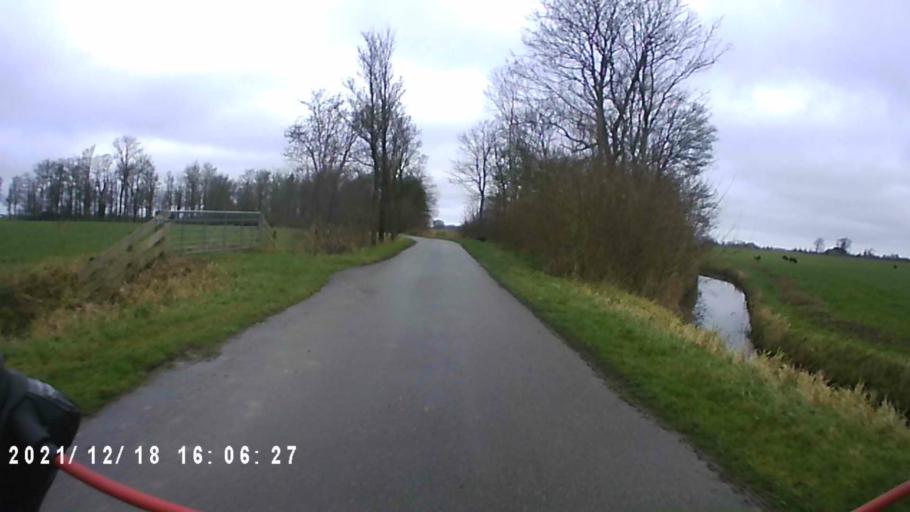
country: NL
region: Friesland
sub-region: Gemeente Dongeradeel
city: Anjum
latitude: 53.3565
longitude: 6.0772
